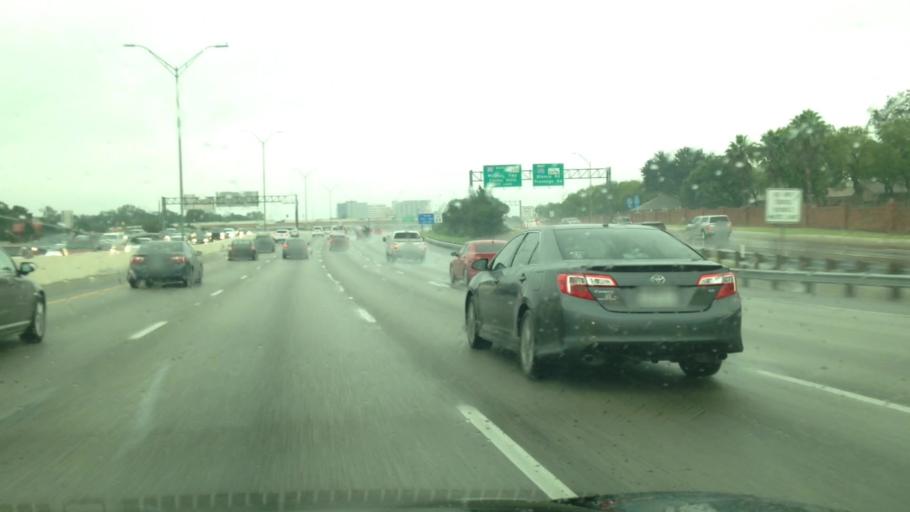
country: US
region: Texas
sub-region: Bexar County
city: Castle Hills
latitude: 29.5198
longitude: -98.5177
